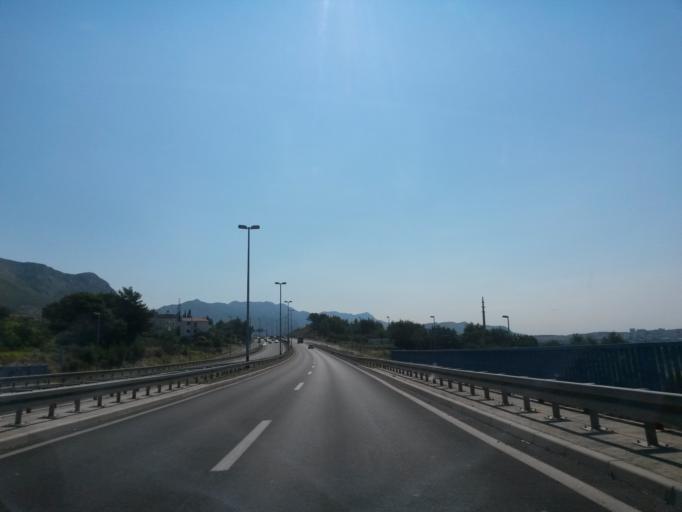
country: HR
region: Splitsko-Dalmatinska
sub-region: Grad Split
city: Split
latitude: 43.5514
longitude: 16.4127
